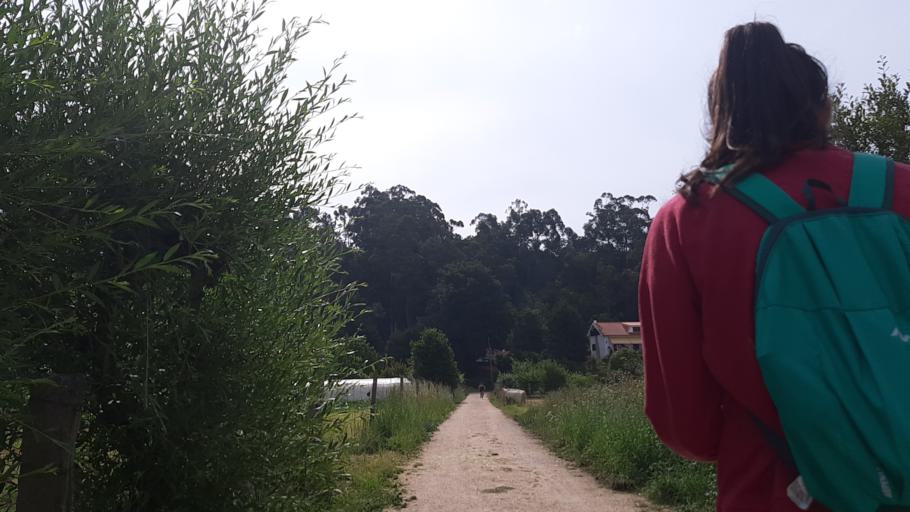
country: ES
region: Galicia
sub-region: Provincia de Pontevedra
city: O Rosal
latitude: 41.9185
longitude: -8.8281
